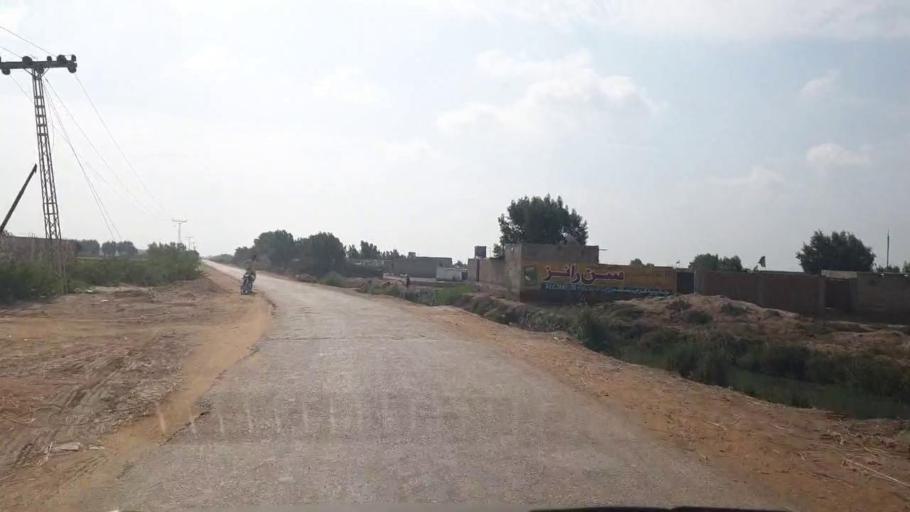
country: PK
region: Sindh
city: Kario
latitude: 24.6464
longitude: 68.5423
